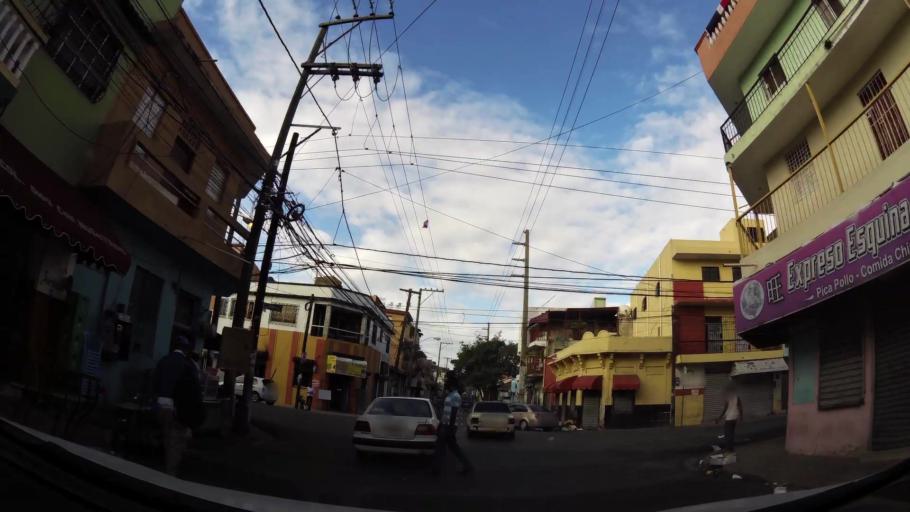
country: DO
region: Nacional
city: San Carlos
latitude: 18.4777
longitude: -69.8892
